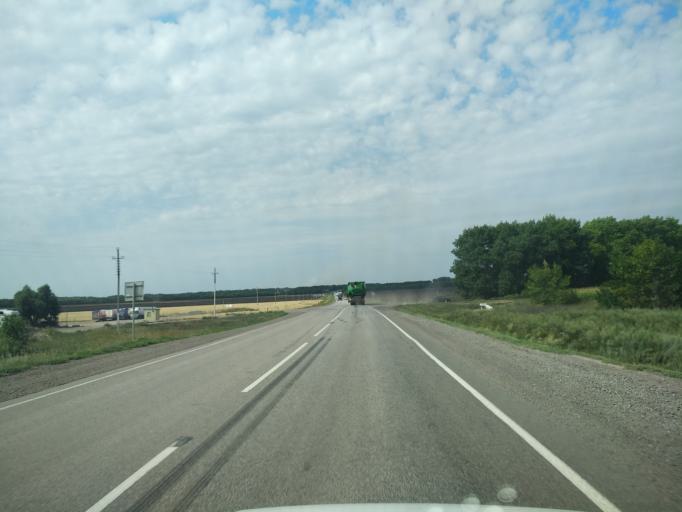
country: RU
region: Lipetsk
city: Dobrinka
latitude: 51.8864
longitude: 40.4298
